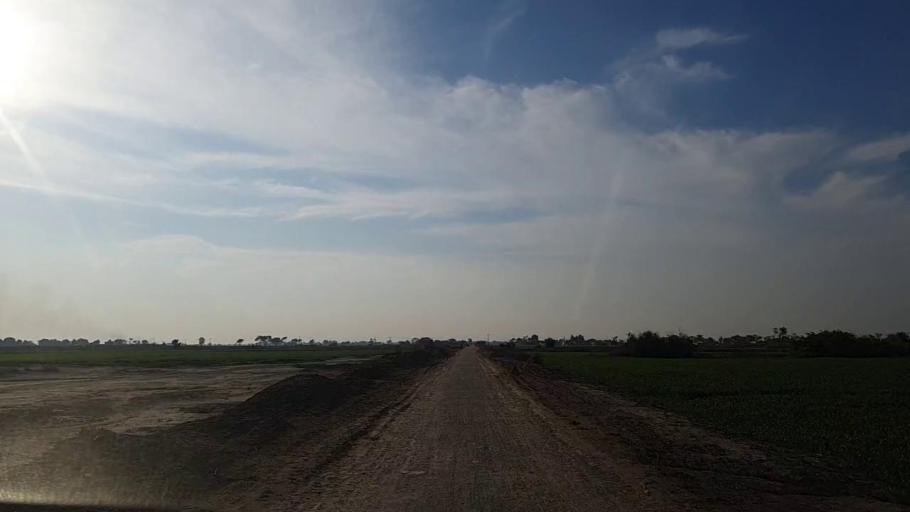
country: PK
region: Sindh
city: Bandhi
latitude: 26.5532
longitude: 68.2561
